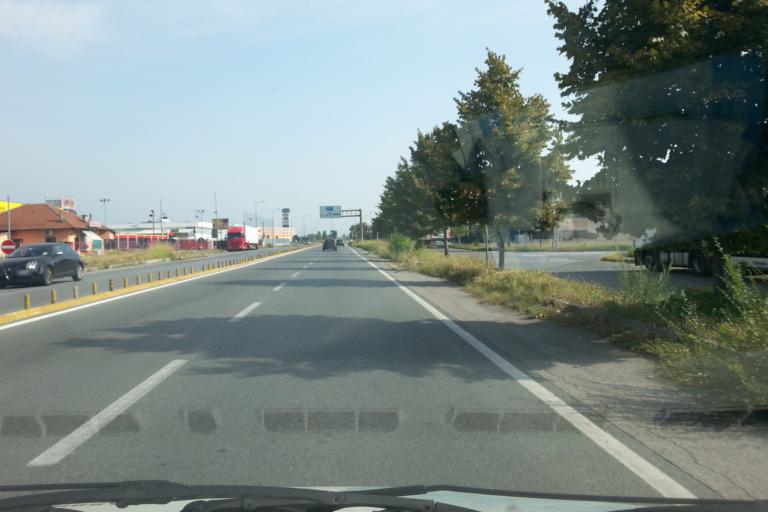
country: IT
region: Piedmont
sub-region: Provincia di Torino
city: Pasta
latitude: 45.0034
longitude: 7.5531
